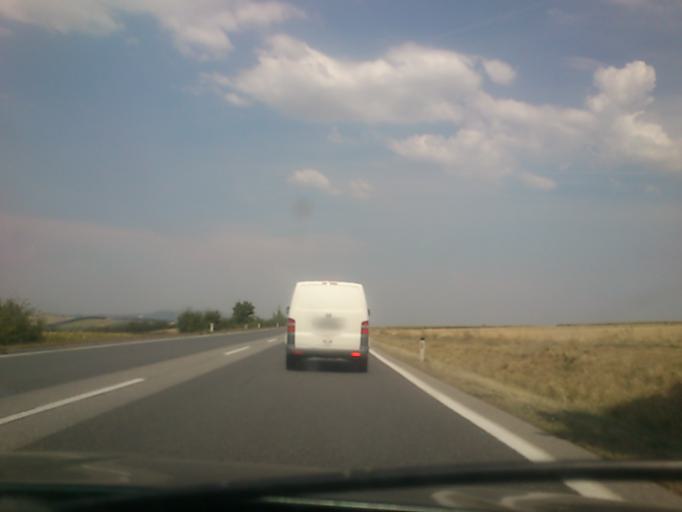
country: AT
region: Lower Austria
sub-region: Politischer Bezirk Mistelbach
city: Drasenhofen
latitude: 48.7106
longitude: 16.6535
